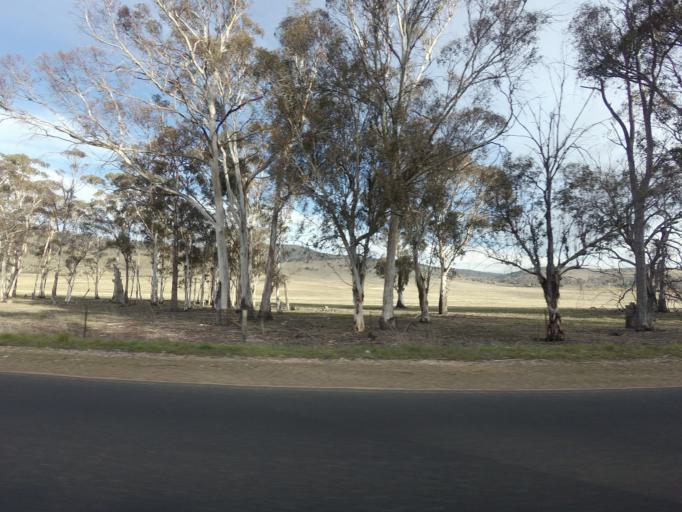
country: AU
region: Tasmania
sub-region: Brighton
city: Bridgewater
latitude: -42.3972
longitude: 147.0729
